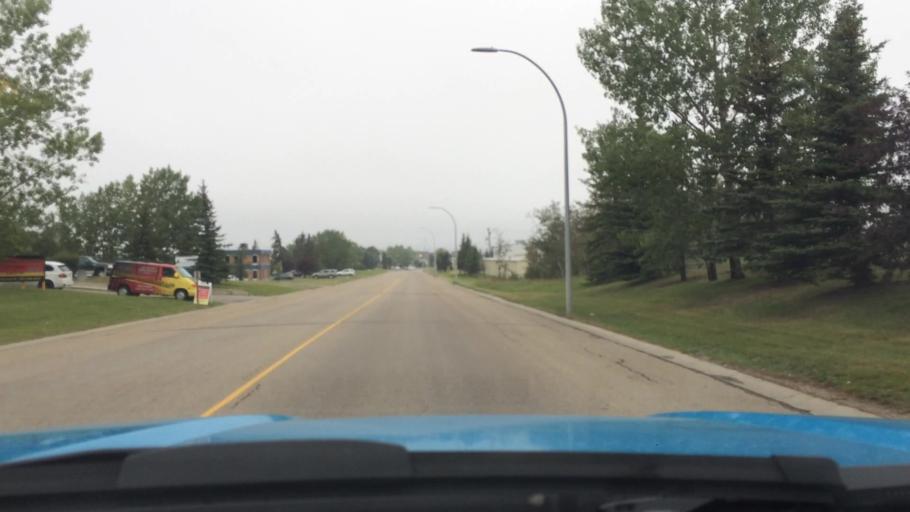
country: CA
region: Alberta
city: Airdrie
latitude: 51.2889
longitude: -113.9834
